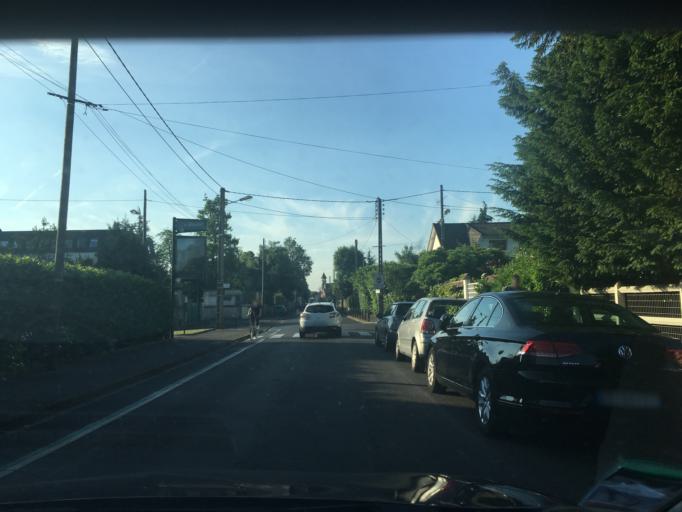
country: FR
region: Ile-de-France
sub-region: Departement de l'Essonne
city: Brunoy
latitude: 48.6960
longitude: 2.4878
